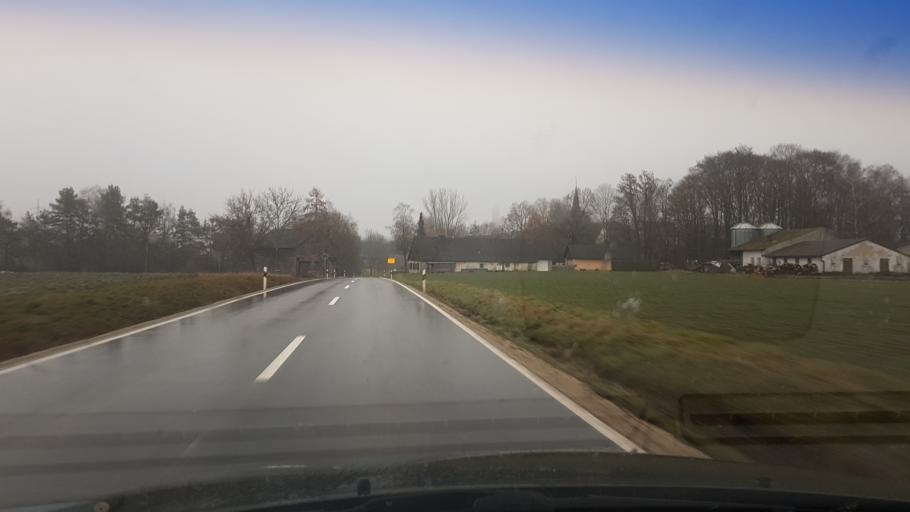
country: DE
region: Bavaria
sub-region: Upper Franconia
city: Wonsees
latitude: 50.0278
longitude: 11.2979
